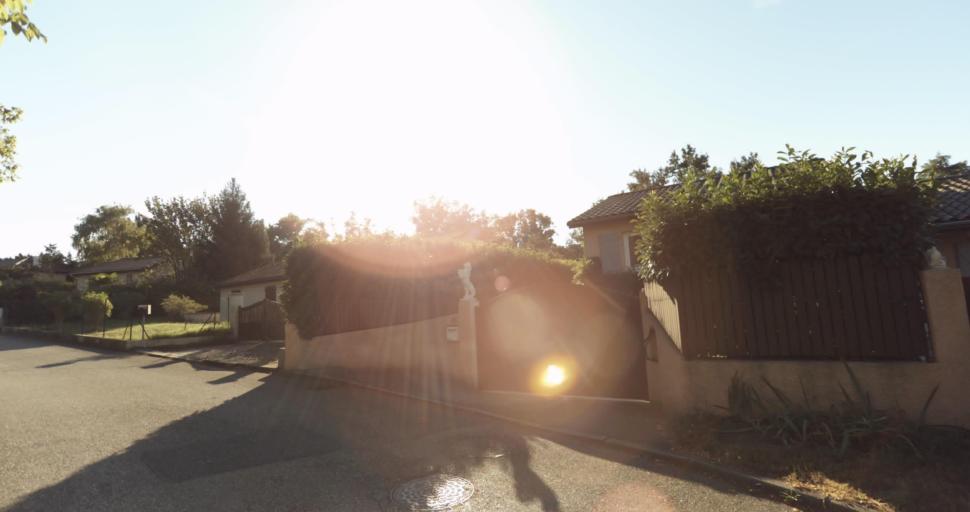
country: FR
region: Rhone-Alpes
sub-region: Departement du Rhone
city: Neuville-sur-Saone
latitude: 45.8829
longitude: 4.8434
